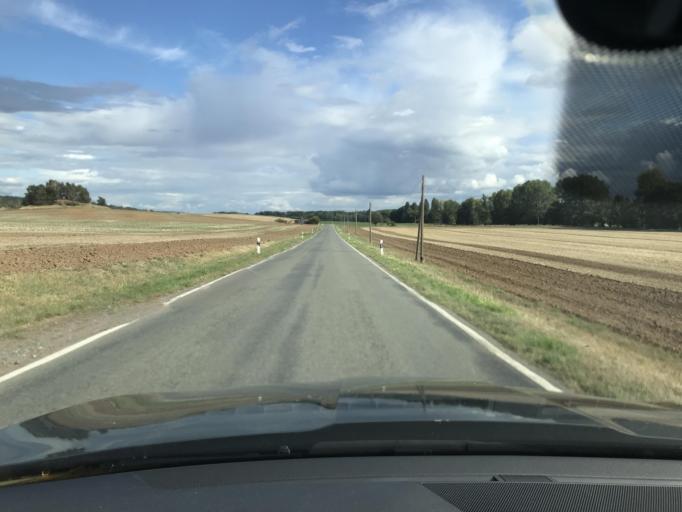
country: DE
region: Saxony-Anhalt
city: Weddersleben
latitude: 51.7793
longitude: 11.0842
